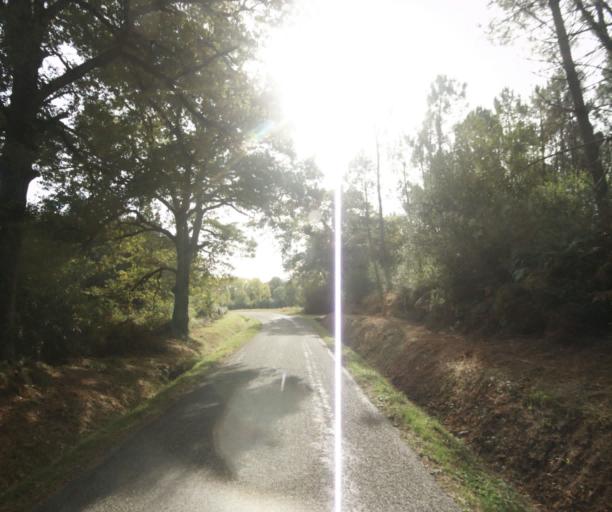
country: FR
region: Midi-Pyrenees
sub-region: Departement du Gers
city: Eauze
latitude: 43.9345
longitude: 0.1042
